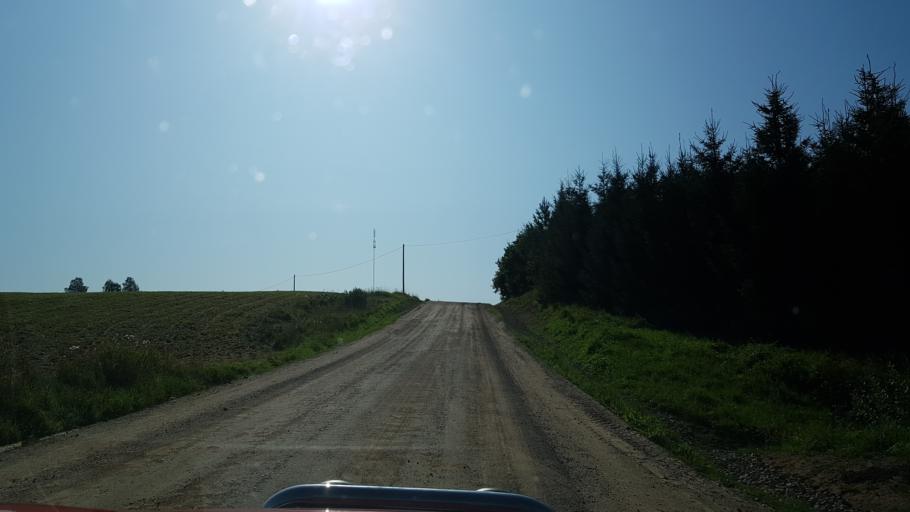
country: LV
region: Apes Novads
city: Ape
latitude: 57.6064
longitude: 26.8436
